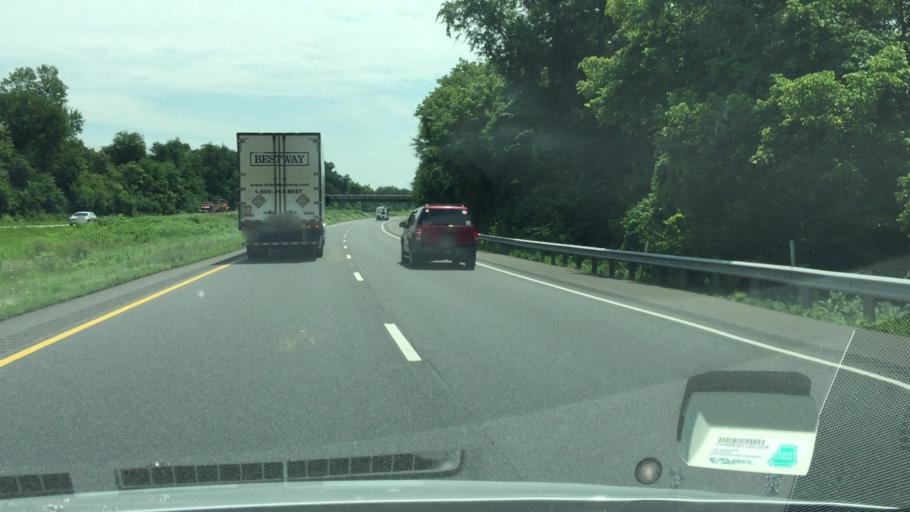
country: US
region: Maryland
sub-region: Washington County
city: Hancock
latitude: 39.6395
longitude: -78.0294
